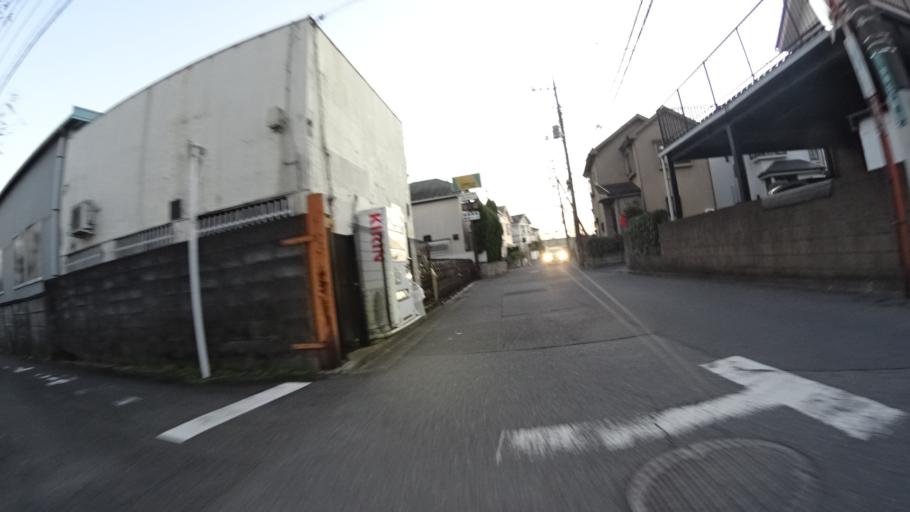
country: JP
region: Tokyo
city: Hino
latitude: 35.6808
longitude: 139.4242
